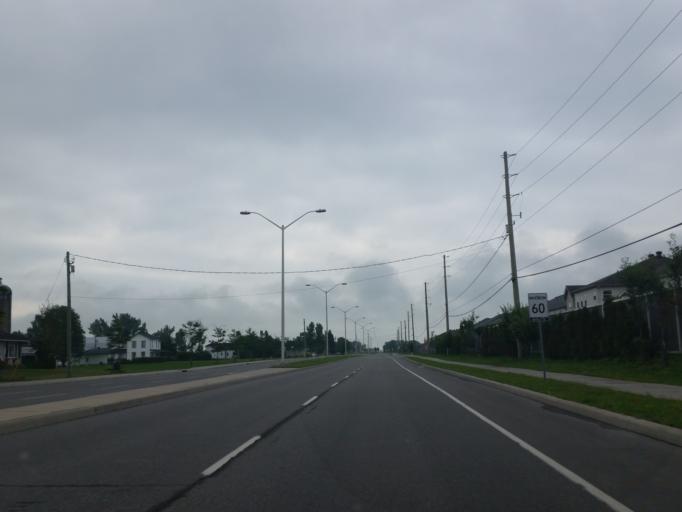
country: CA
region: Ontario
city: Clarence-Rockland
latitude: 45.4624
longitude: -75.4498
